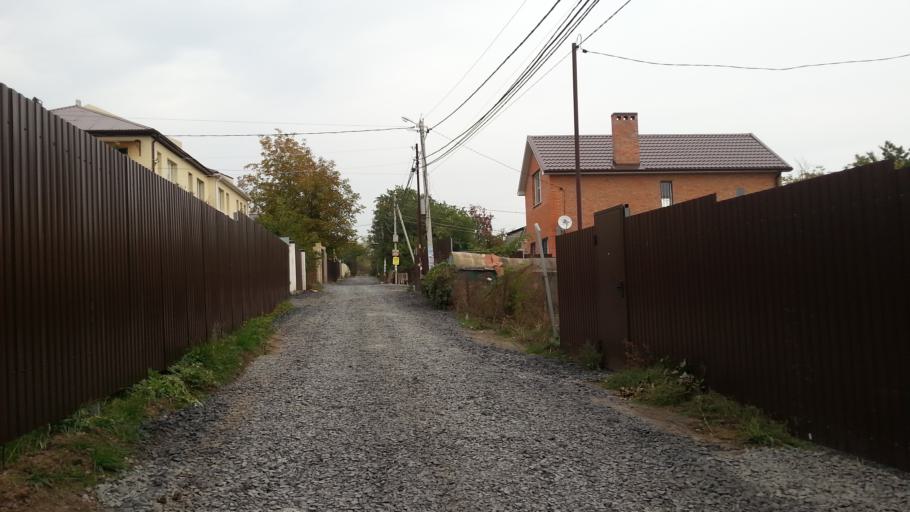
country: RU
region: Rostov
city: Severnyy
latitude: 47.2945
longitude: 39.6674
